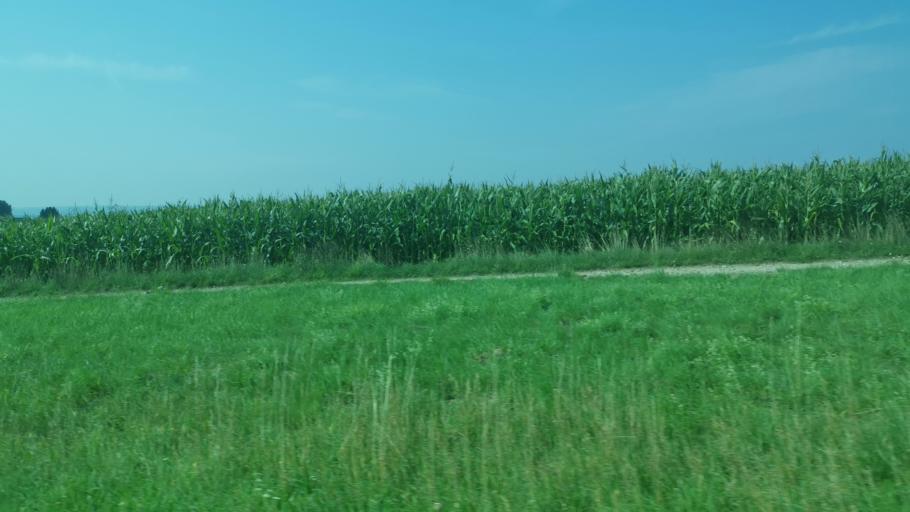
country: DE
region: Bavaria
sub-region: Upper Palatinate
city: Pemfling
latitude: 49.2575
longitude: 12.6387
